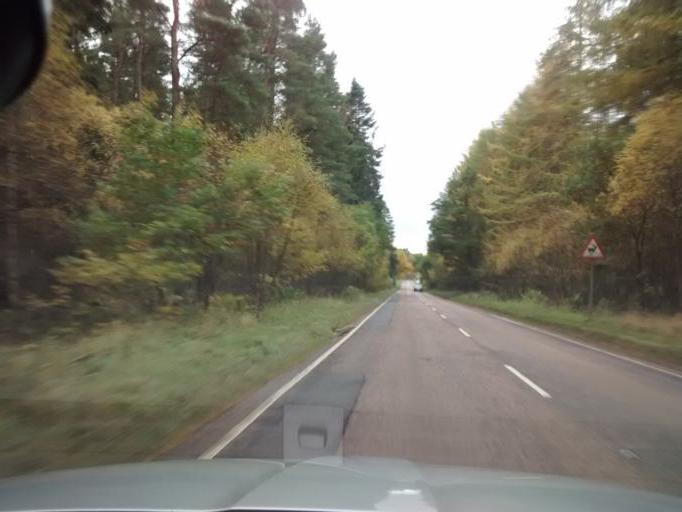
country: GB
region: Scotland
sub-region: Perth and Kinross
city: Blairgowrie
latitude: 56.5430
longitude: -3.3572
